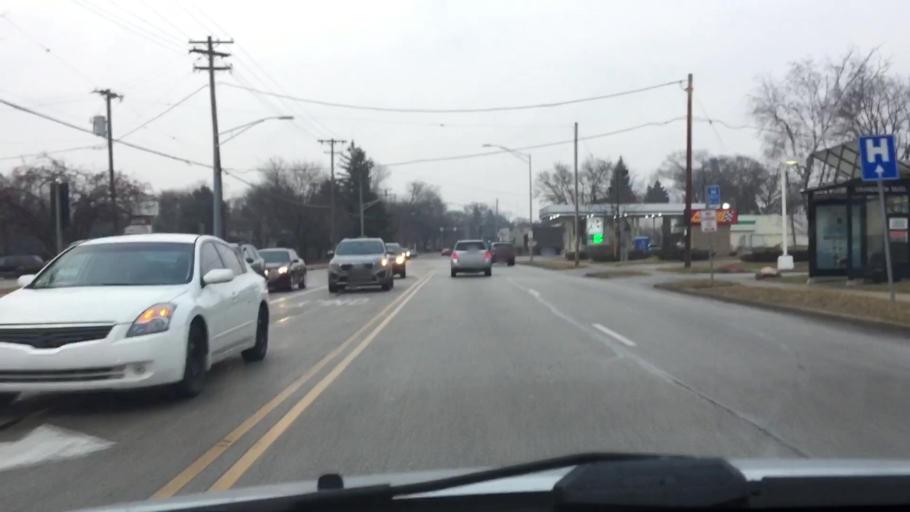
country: US
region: Wisconsin
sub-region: Waukesha County
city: Waukesha
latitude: 43.0218
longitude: -88.2556
